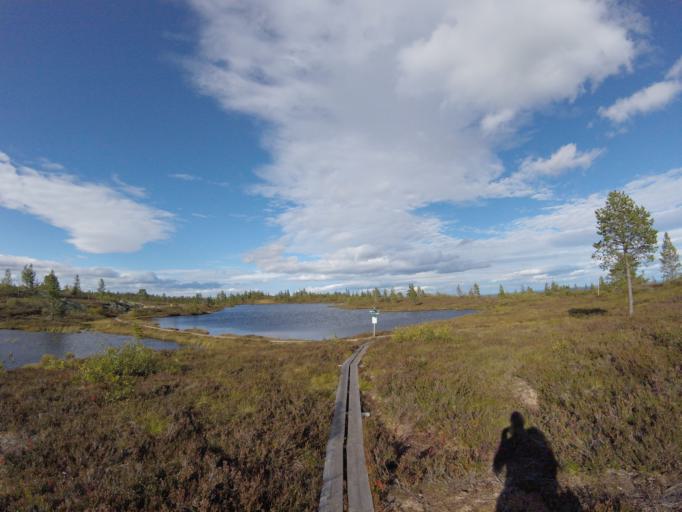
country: NO
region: Buskerud
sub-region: Flesberg
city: Lampeland
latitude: 59.7724
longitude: 9.4069
